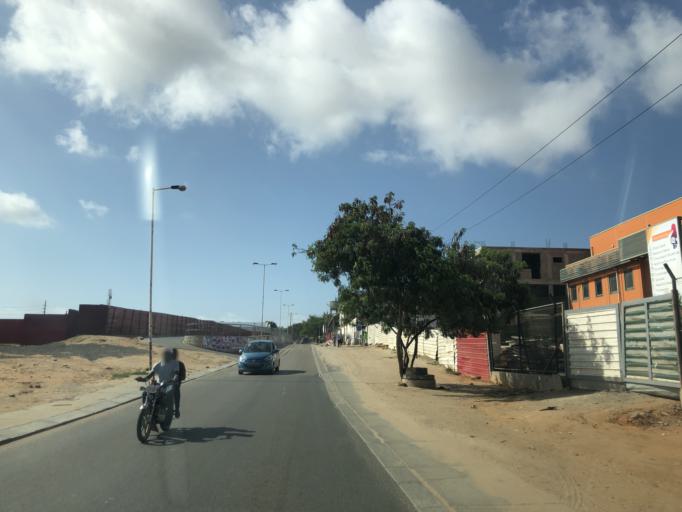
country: AO
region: Luanda
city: Luanda
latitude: -8.9102
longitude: 13.2345
